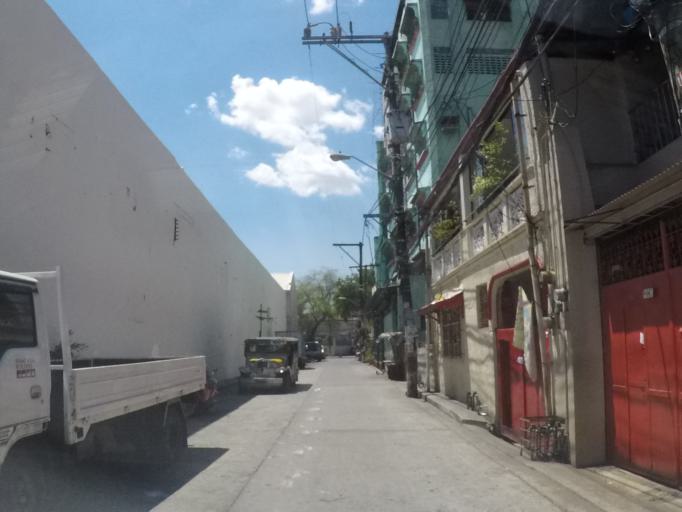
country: PH
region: Metro Manila
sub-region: San Juan
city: San Juan
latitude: 14.5972
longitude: 121.0275
